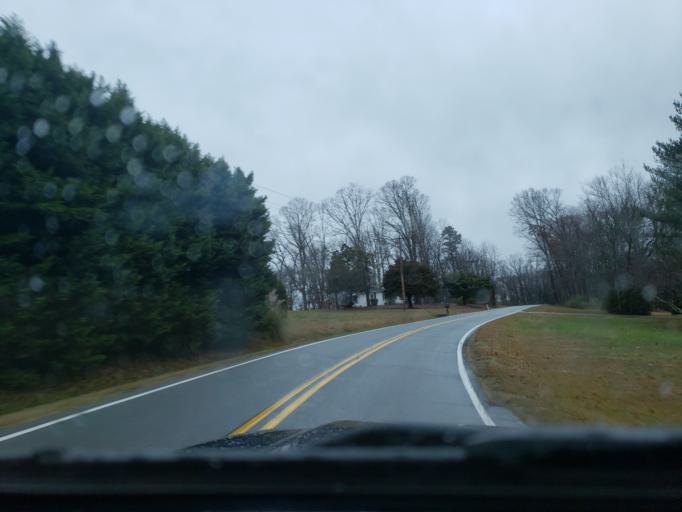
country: US
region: North Carolina
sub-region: Cleveland County
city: White Plains
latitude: 35.1910
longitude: -81.3786
